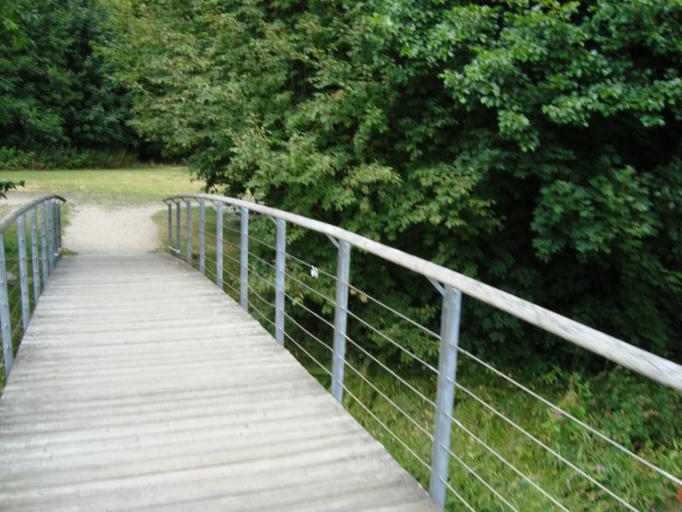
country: DE
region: Bavaria
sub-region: Upper Franconia
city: Marktredwitz
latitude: 49.9967
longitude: 12.0833
